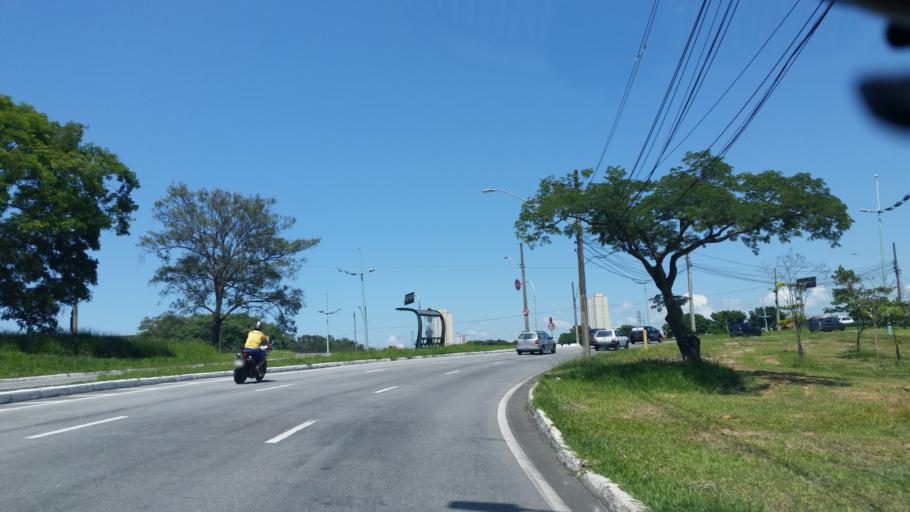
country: BR
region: Sao Paulo
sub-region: Sao Jose Dos Campos
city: Sao Jose dos Campos
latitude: -23.1804
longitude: -45.8387
